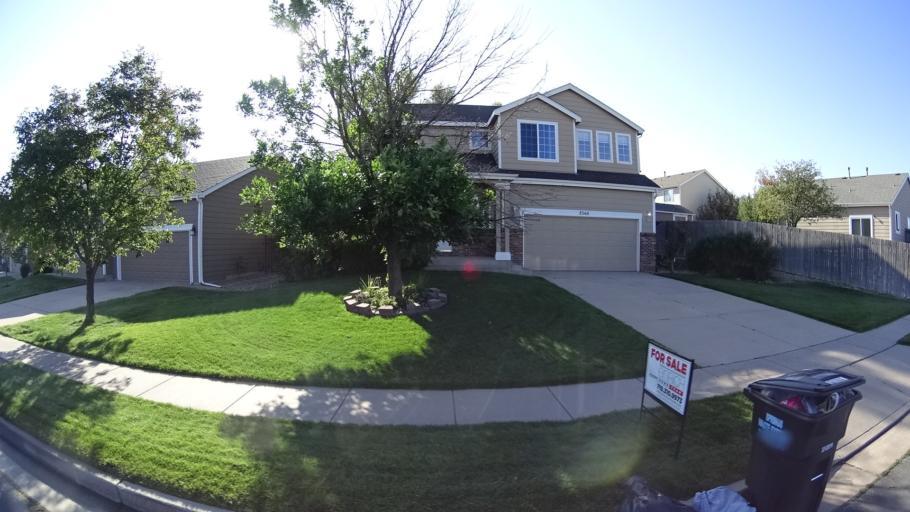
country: US
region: Colorado
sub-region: El Paso County
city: Cimarron Hills
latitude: 38.8840
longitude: -104.6960
